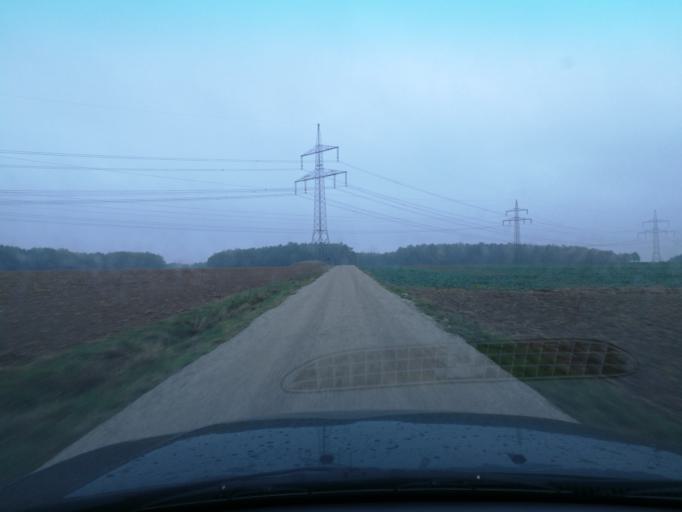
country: DE
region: Bavaria
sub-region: Regierungsbezirk Mittelfranken
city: Obermichelbach
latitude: 49.5394
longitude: 10.9068
